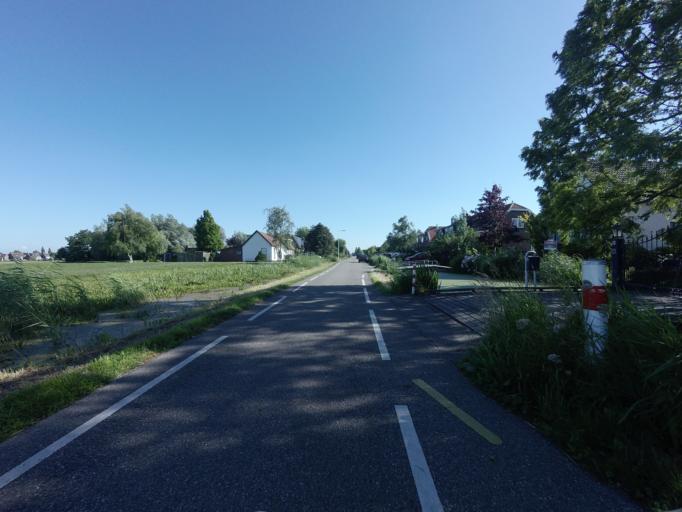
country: NL
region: South Holland
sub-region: Gemeente Waddinxveen
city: Vondelwijk
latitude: 52.0612
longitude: 4.6828
